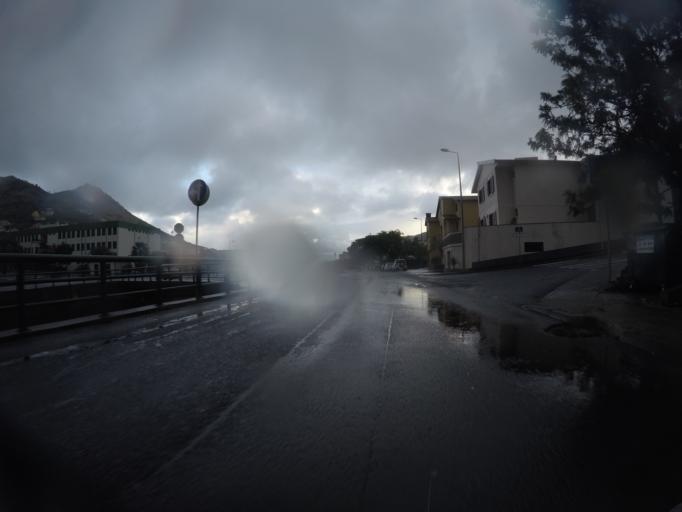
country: PT
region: Madeira
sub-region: Machico
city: Machico
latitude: 32.7260
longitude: -16.7723
